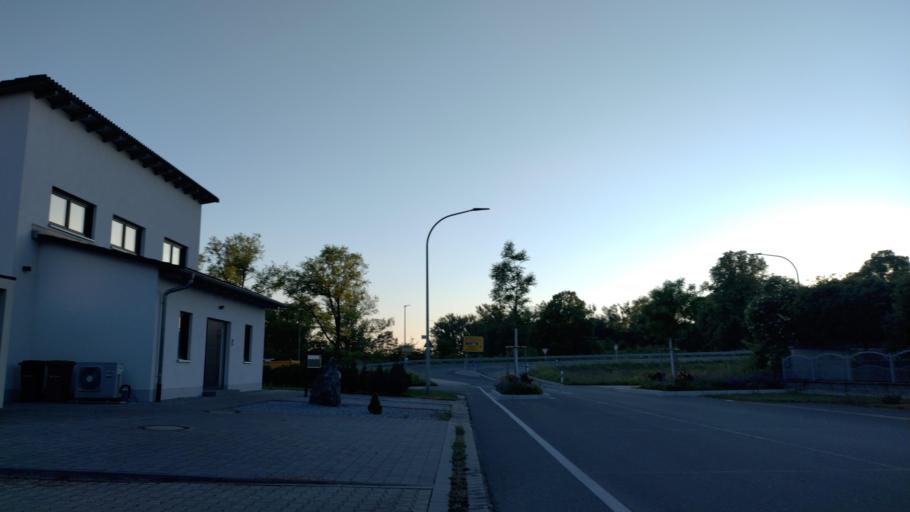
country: DE
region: Bavaria
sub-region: Upper Franconia
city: Bindlach
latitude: 49.9942
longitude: 11.6242
